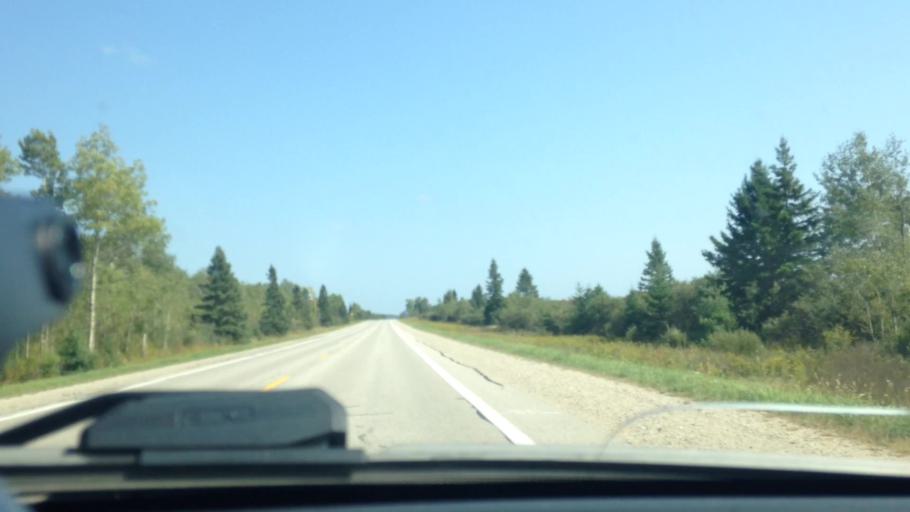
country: US
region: Michigan
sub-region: Luce County
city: Newberry
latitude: 46.3103
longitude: -85.6059
